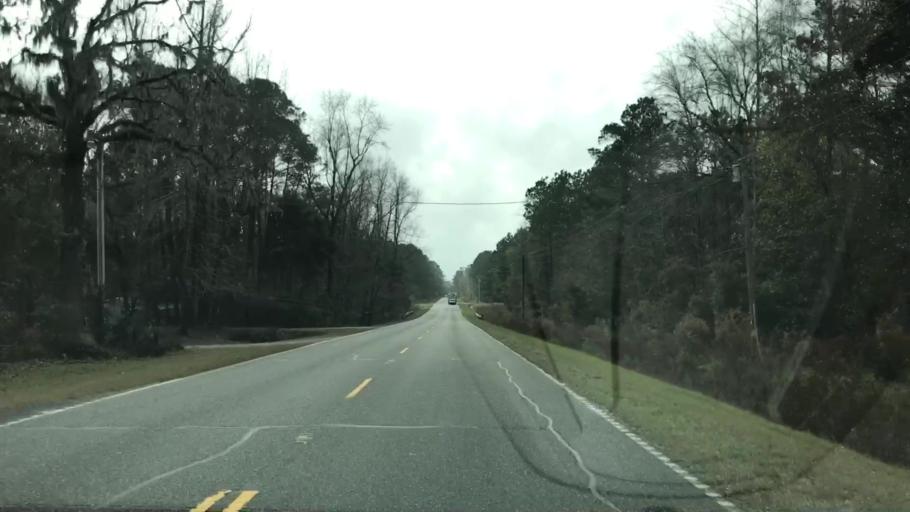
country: US
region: South Carolina
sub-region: Georgetown County
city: Murrells Inlet
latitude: 33.6474
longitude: -79.1718
